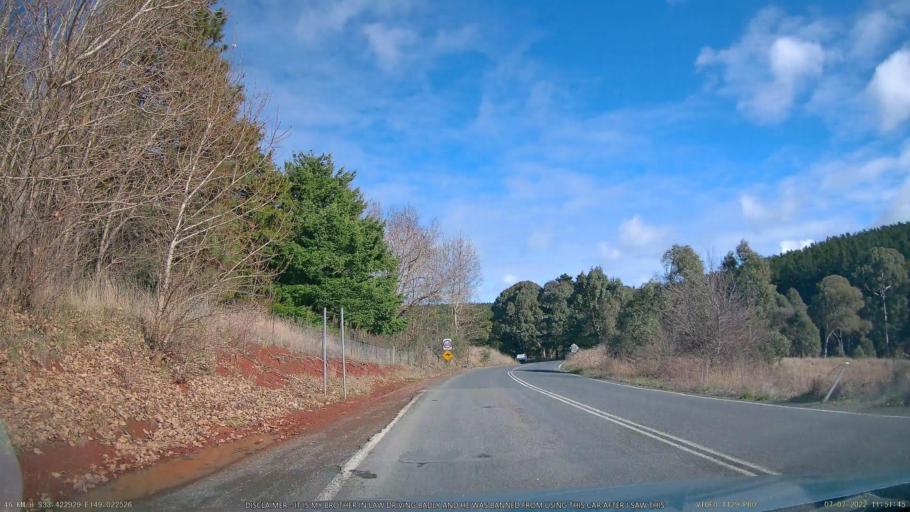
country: AU
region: New South Wales
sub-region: Orange Municipality
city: Orange
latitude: -33.4229
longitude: 149.0221
